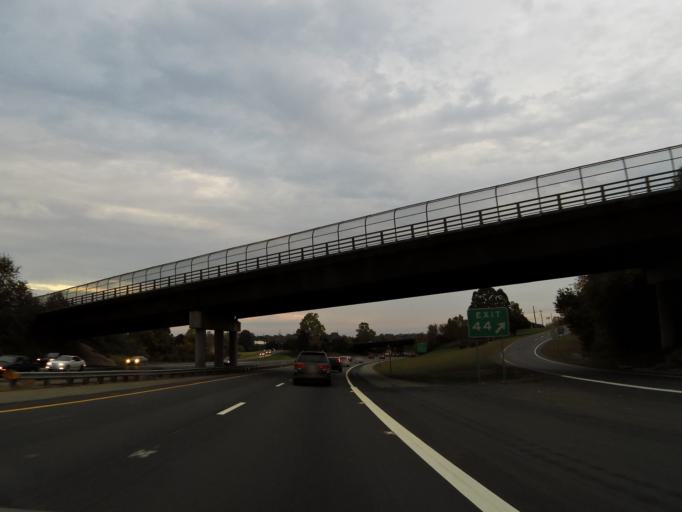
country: US
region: North Carolina
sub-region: Catawba County
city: Hickory
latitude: 35.7247
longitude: -81.3576
